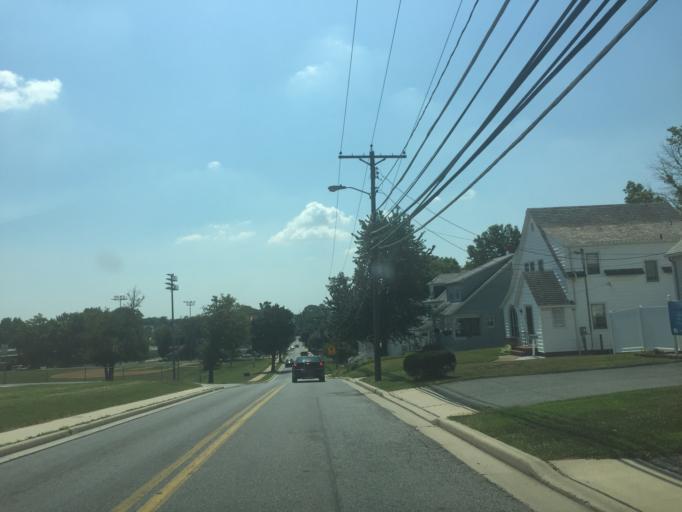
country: US
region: Maryland
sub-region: Baltimore County
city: Overlea
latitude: 39.3613
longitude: -76.5224
